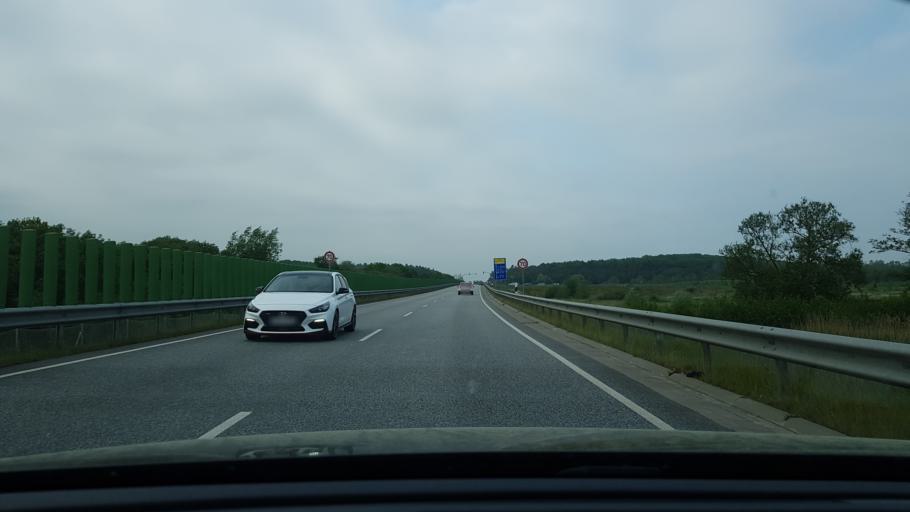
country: DE
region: Schleswig-Holstein
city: Gross Sarau
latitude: 53.7802
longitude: 10.7056
